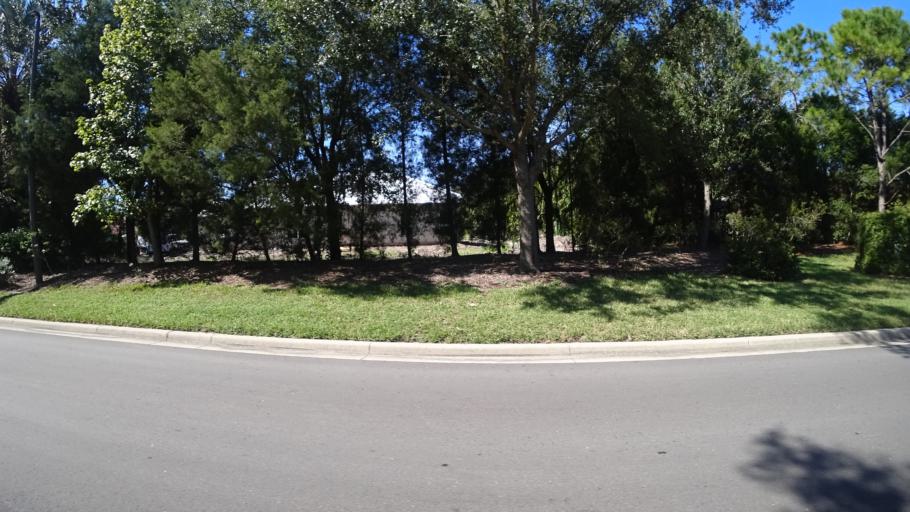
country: US
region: Florida
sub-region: Sarasota County
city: The Meadows
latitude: 27.4132
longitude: -82.4154
